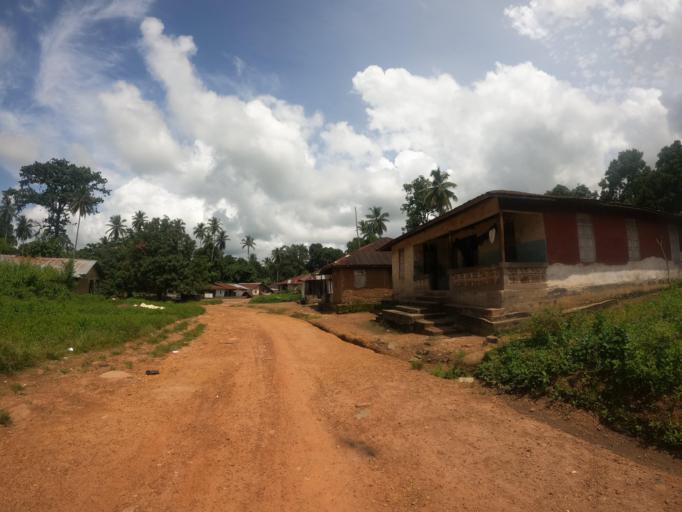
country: SL
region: Northern Province
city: Makeni
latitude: 8.8993
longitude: -12.0592
